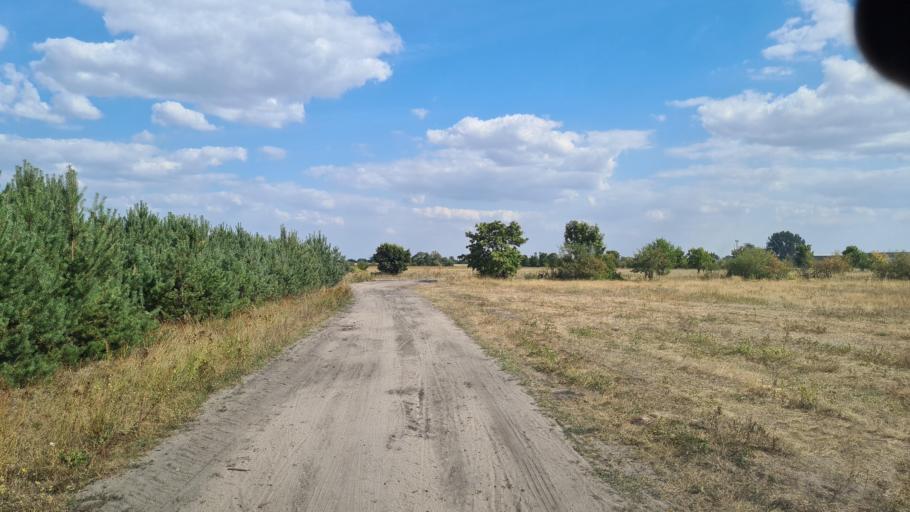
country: DE
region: Saxony-Anhalt
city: Elster
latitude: 51.8436
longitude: 12.8052
